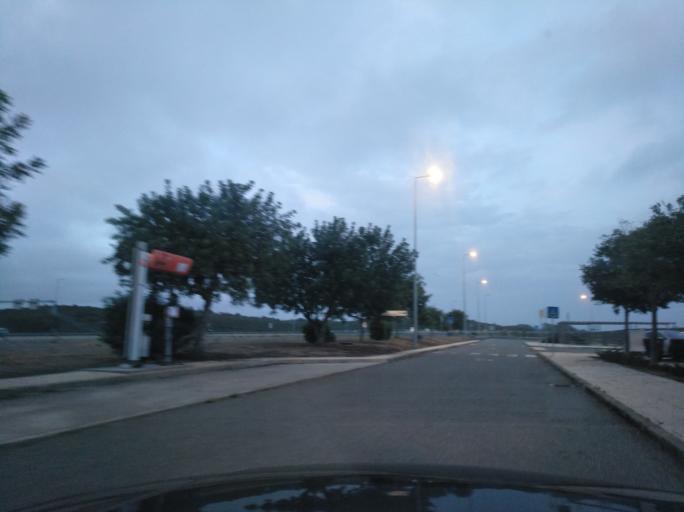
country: PT
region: Faro
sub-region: Lagos
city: Lagos
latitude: 37.1484
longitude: -8.7030
